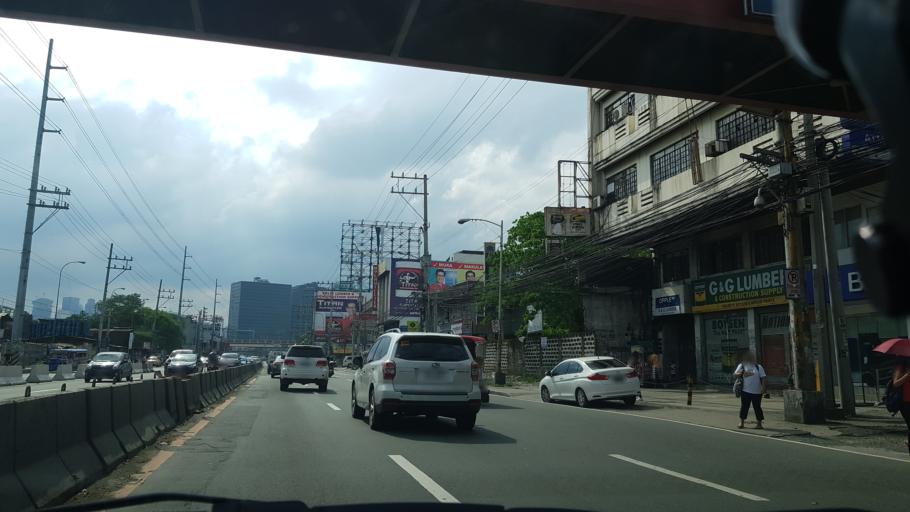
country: PH
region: Metro Manila
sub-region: Pasig
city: Pasig City
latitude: 14.5904
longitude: 121.0895
